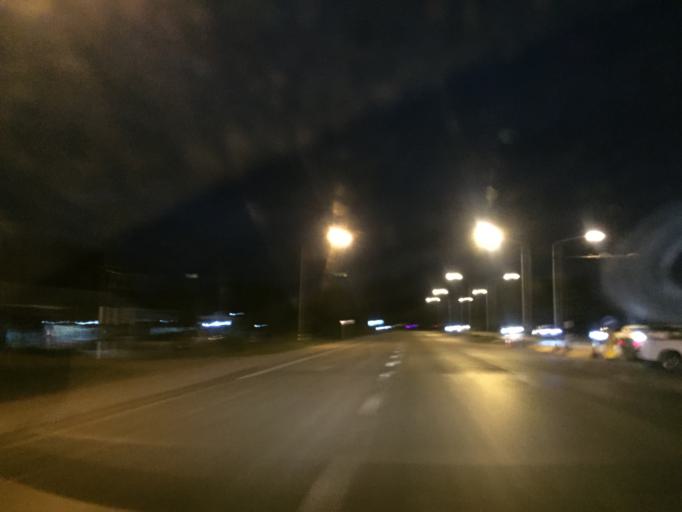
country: TH
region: Changwat Nong Bua Lamphu
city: Na Klang
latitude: 17.2934
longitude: 102.2542
